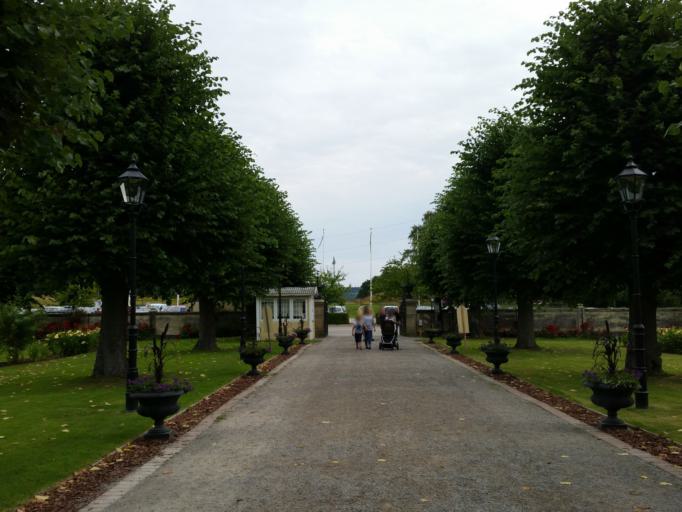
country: SE
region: Stockholm
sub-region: Botkyrka Kommun
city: Tumba
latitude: 59.2208
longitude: 17.8314
